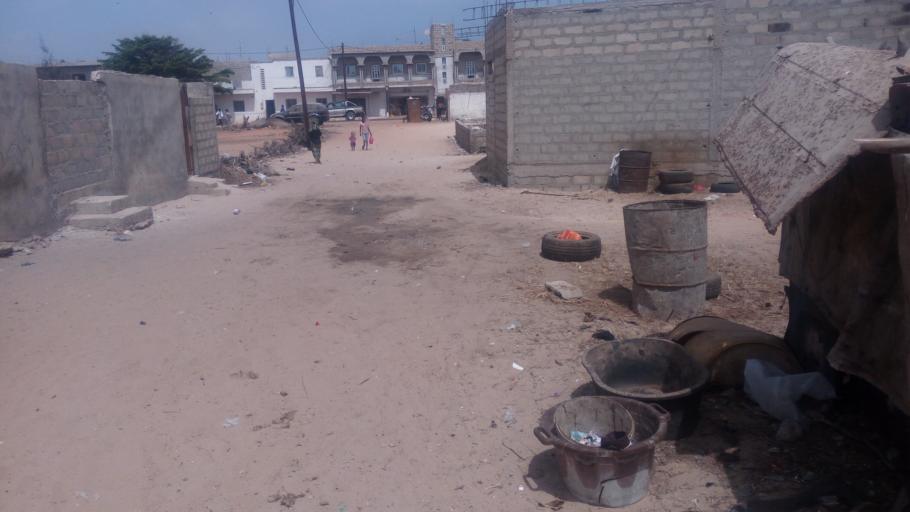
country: SN
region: Dakar
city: Pikine
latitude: 14.7985
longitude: -17.3363
